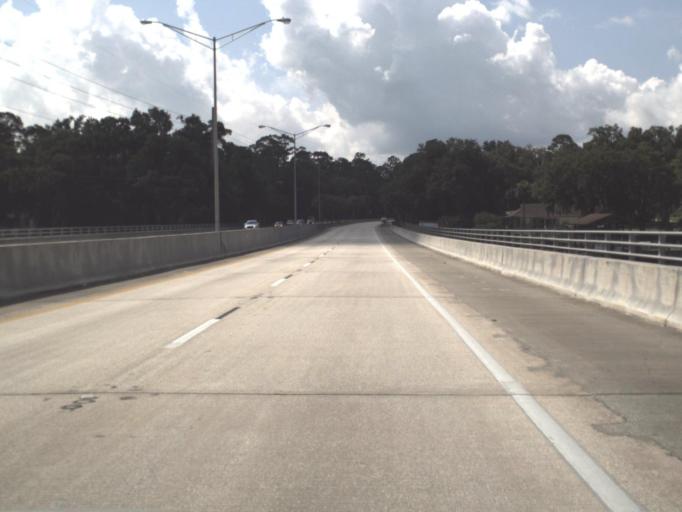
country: US
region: Florida
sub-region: Saint Johns County
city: Fruit Cove
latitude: 30.1300
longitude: -81.6279
